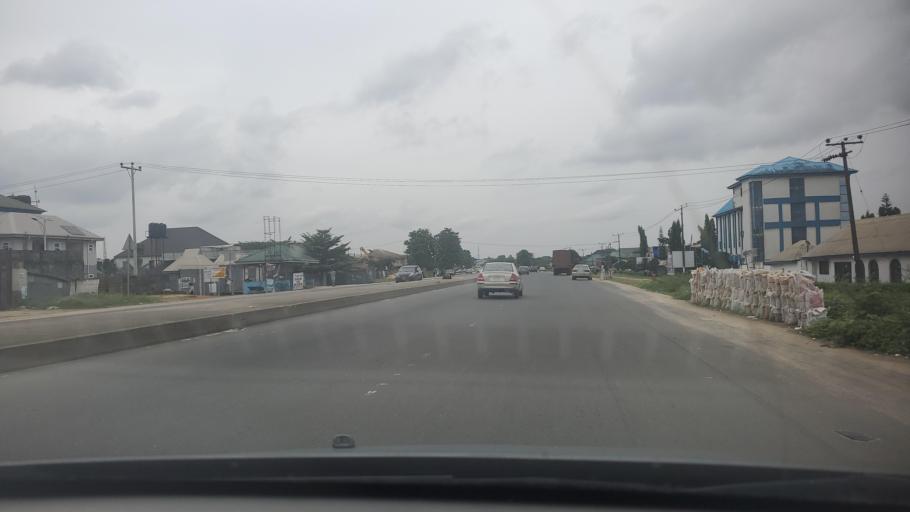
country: NG
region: Rivers
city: Emuoha
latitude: 4.8720
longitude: 6.9627
